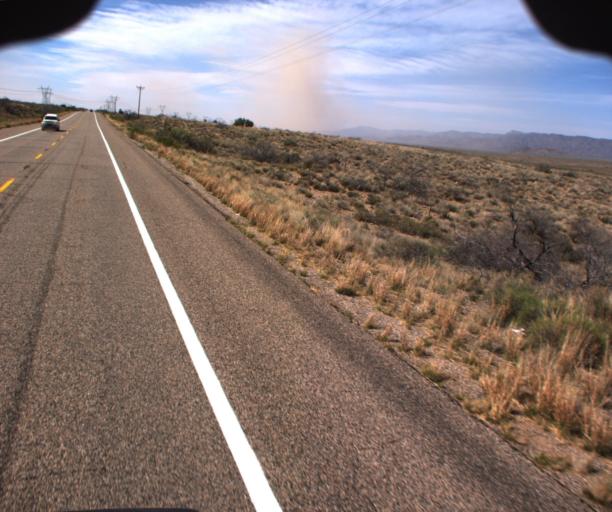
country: US
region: Arizona
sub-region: Mohave County
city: New Kingman-Butler
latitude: 35.3889
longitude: -113.7392
